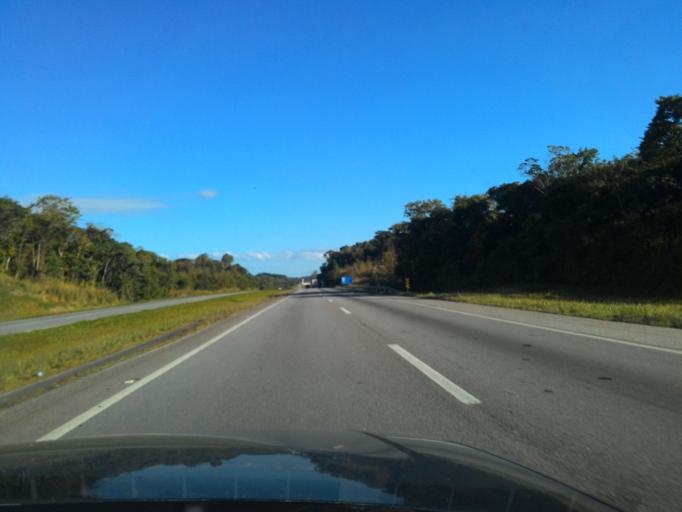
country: BR
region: Sao Paulo
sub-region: Registro
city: Registro
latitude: -24.5403
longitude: -47.8603
